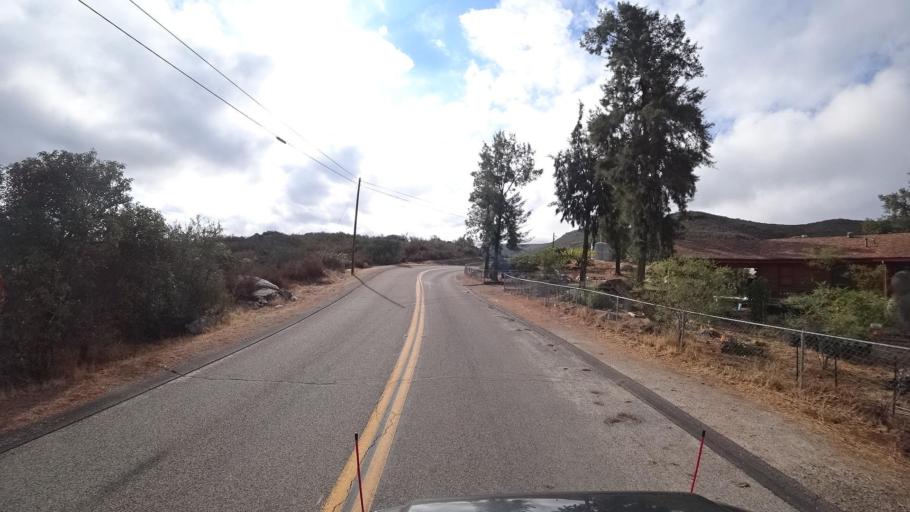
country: MX
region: Baja California
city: Tecate
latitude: 32.6313
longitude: -116.6344
